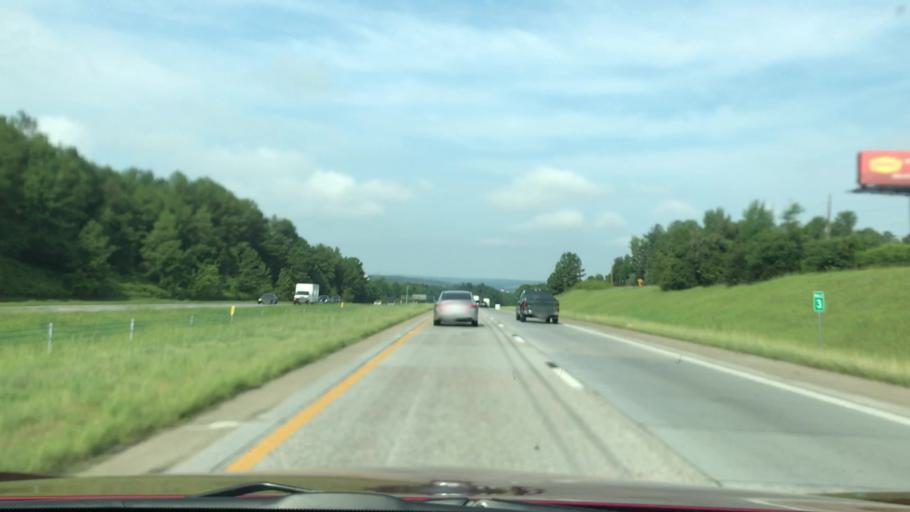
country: US
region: South Carolina
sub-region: Aiken County
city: Belvedere
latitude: 33.5477
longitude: -81.9622
